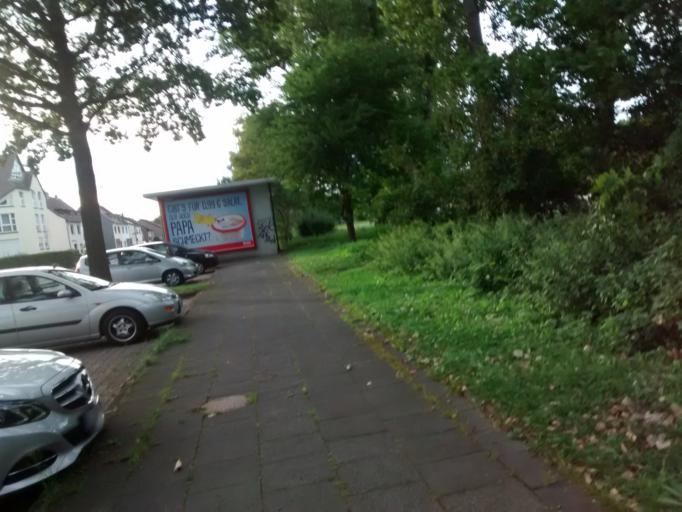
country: DE
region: North Rhine-Westphalia
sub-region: Regierungsbezirk Koln
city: Merheim
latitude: 50.9813
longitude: 7.0454
